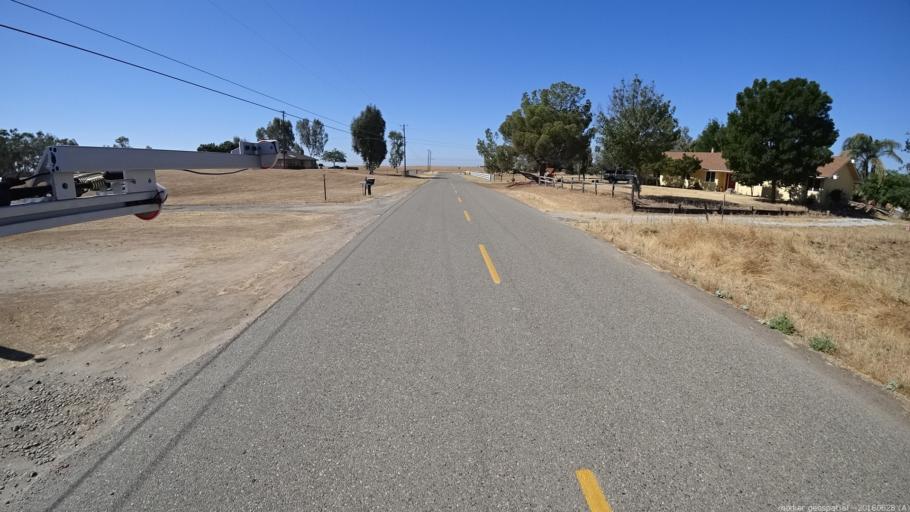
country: US
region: California
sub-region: Madera County
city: Bonadelle Ranchos-Madera Ranchos
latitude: 36.9977
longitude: -119.8612
